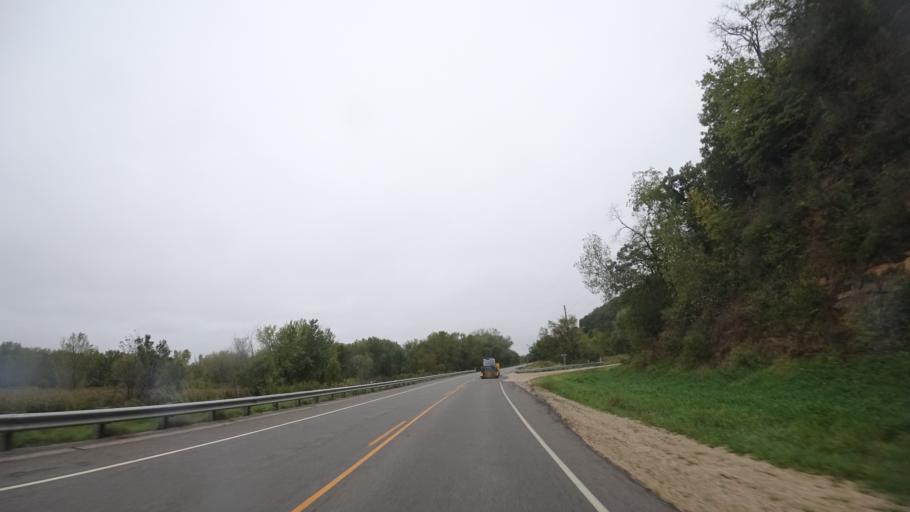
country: US
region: Wisconsin
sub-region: Crawford County
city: Prairie du Chien
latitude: 43.0613
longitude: -90.9547
